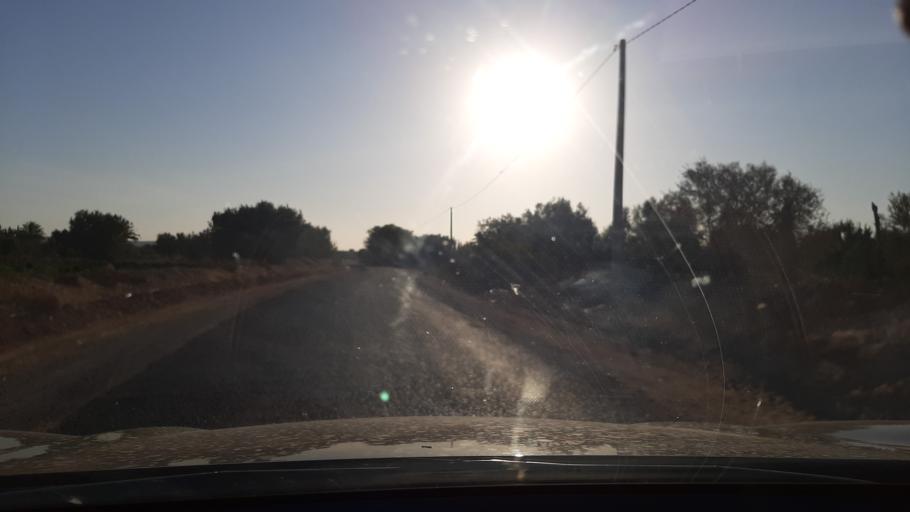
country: TN
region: Qabis
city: Matmata
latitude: 33.6175
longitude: 10.2555
